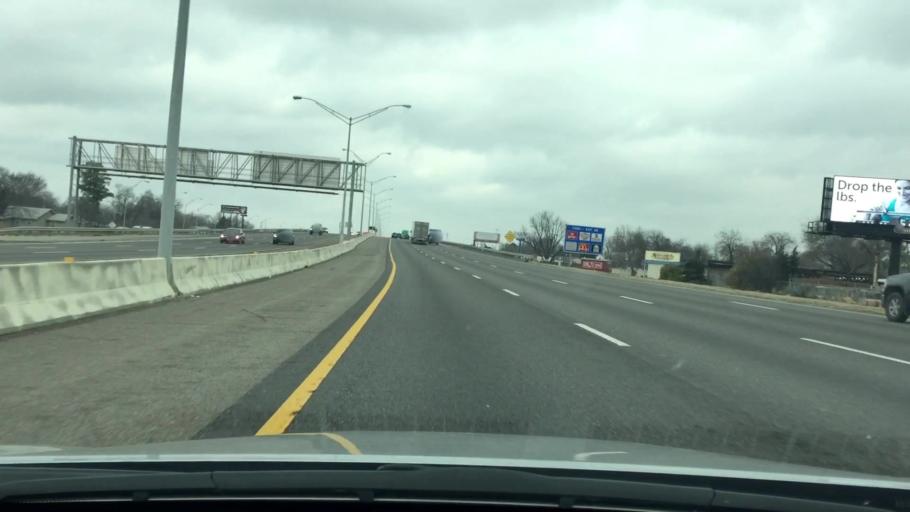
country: US
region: Oklahoma
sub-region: Cleveland County
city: Moore
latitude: 35.3358
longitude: -97.4906
